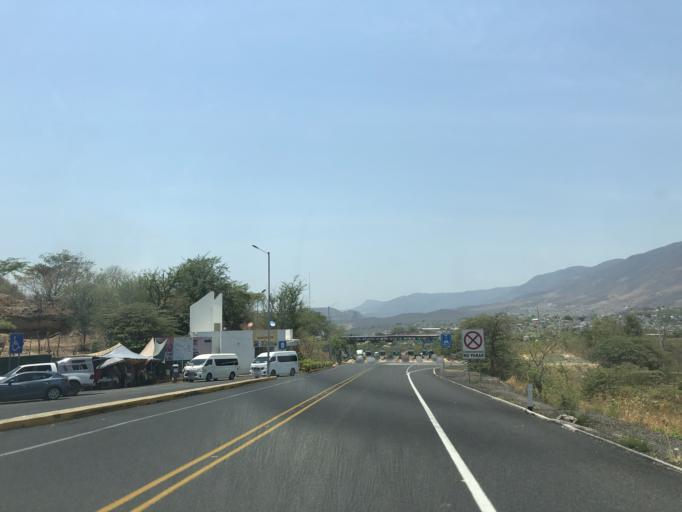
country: MX
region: Chiapas
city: Chiapa de Corzo
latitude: 16.7294
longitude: -93.0080
